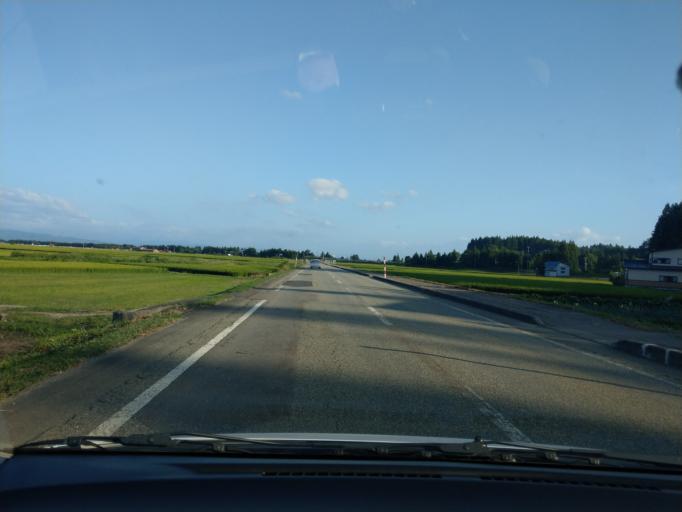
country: JP
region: Akita
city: Omagari
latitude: 39.4128
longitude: 140.4442
